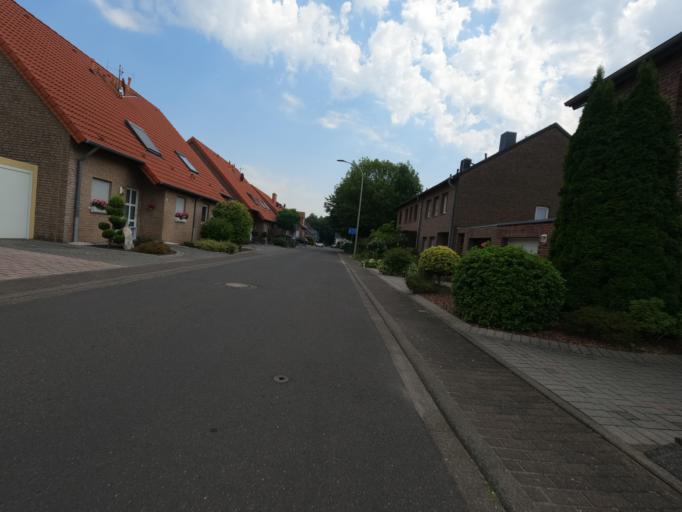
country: DE
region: North Rhine-Westphalia
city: Baesweiler
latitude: 50.9165
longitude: 6.1922
